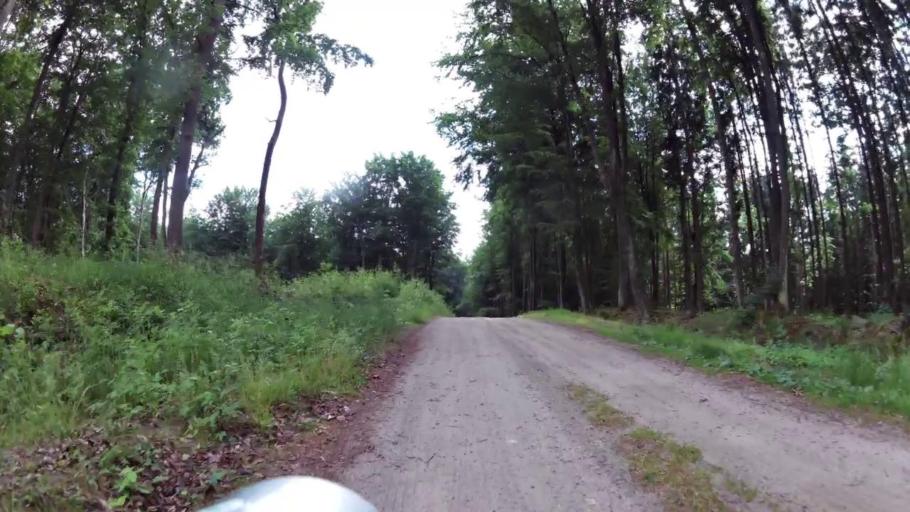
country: PL
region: West Pomeranian Voivodeship
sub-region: Powiat koszalinski
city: Bobolice
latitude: 53.9493
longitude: 16.6788
